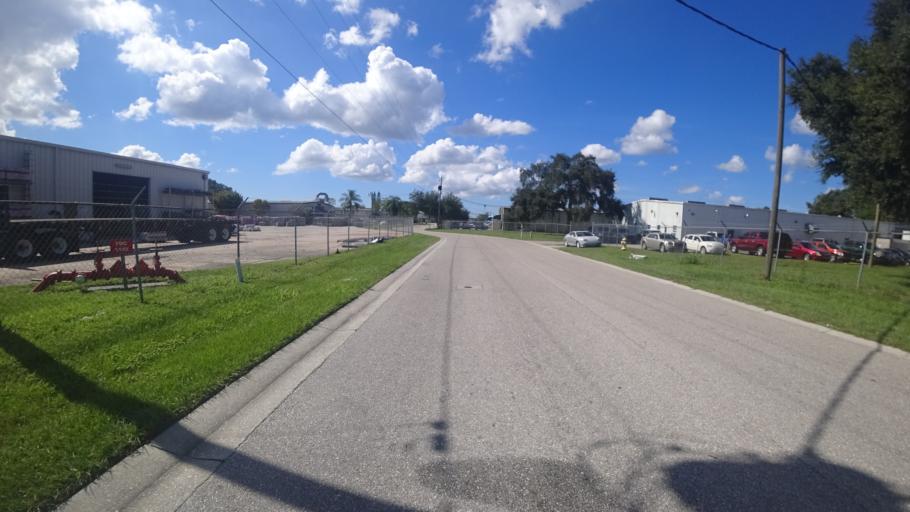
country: US
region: Florida
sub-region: Manatee County
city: Memphis
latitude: 27.5239
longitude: -82.5487
